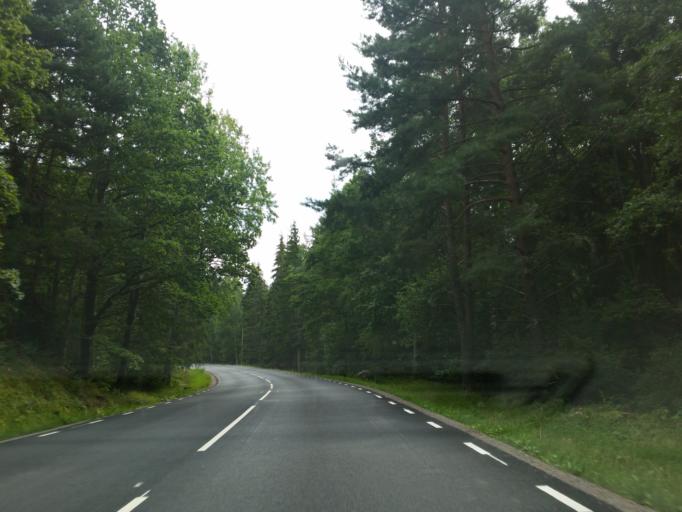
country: SE
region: Soedermanland
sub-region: Strangnas Kommun
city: Mariefred
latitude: 59.2640
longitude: 17.1625
